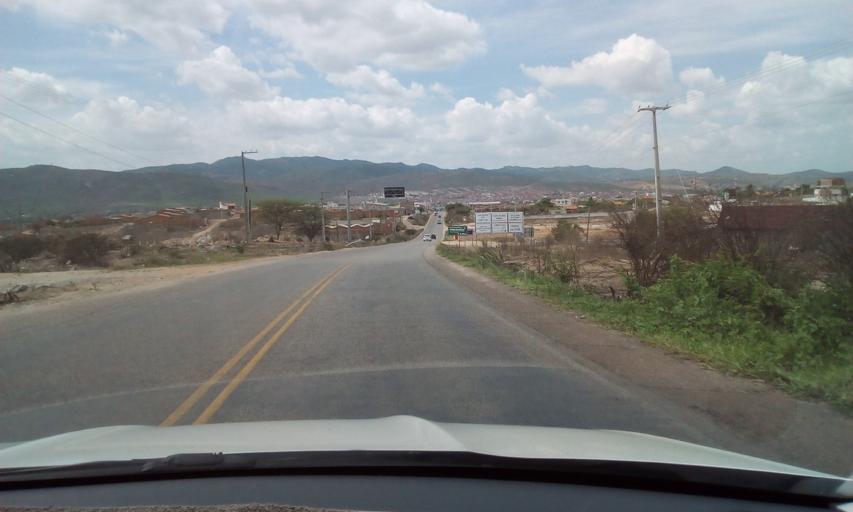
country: BR
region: Pernambuco
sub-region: Bezerros
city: Bezerros
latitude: -8.2590
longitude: -35.7570
